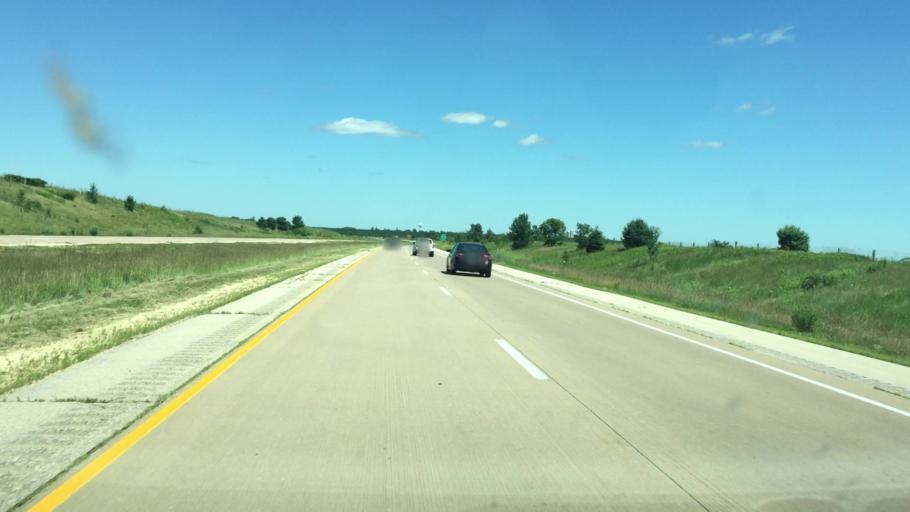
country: US
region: Wisconsin
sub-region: Grant County
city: Platteville
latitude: 42.7395
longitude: -90.3710
